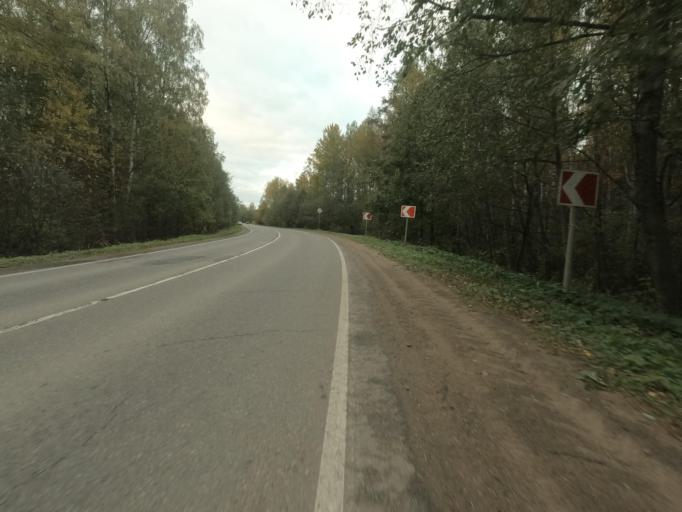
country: RU
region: Leningrad
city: Pavlovo
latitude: 59.8012
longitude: 30.9414
